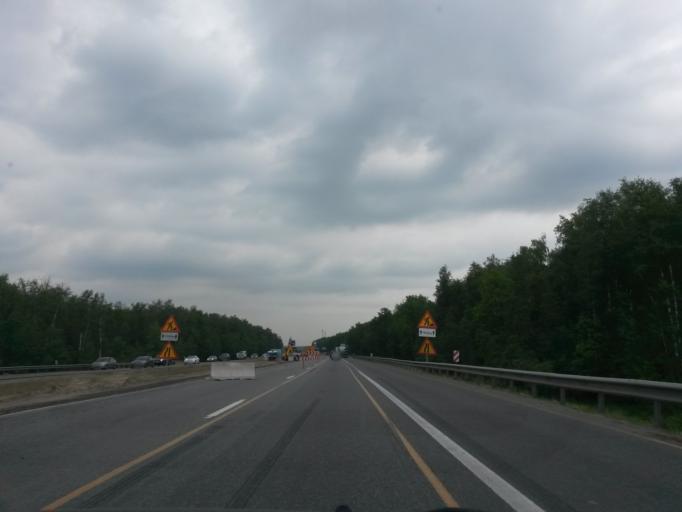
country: RU
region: Moskovskaya
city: Lyubuchany
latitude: 55.2137
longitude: 37.5348
